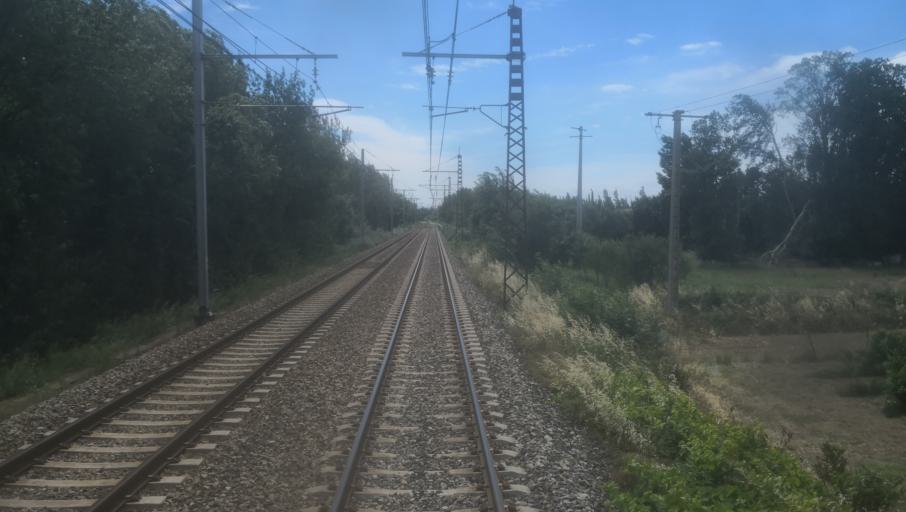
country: FR
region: Languedoc-Roussillon
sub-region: Departement de l'Aude
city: Narbonne
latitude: 43.2053
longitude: 3.0206
